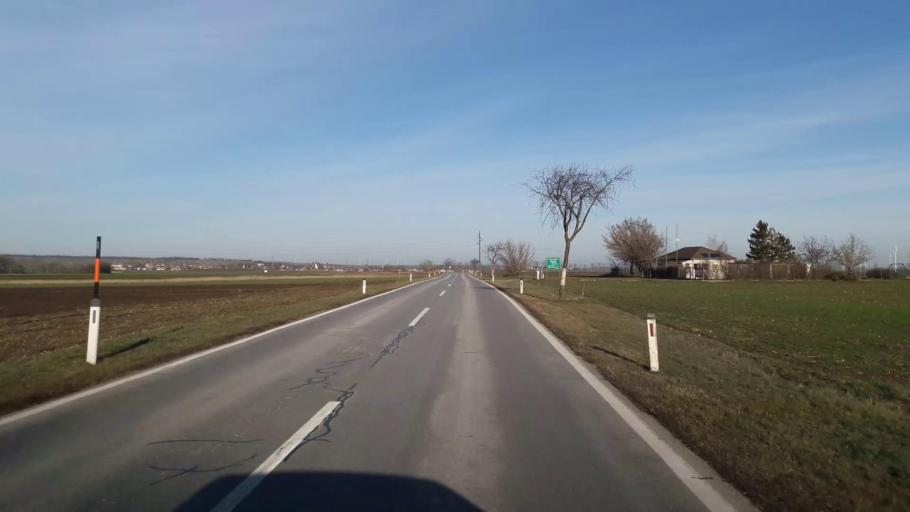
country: AT
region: Lower Austria
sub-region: Politischer Bezirk Mistelbach
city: Gross-Engersdorf
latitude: 48.3316
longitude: 16.5894
